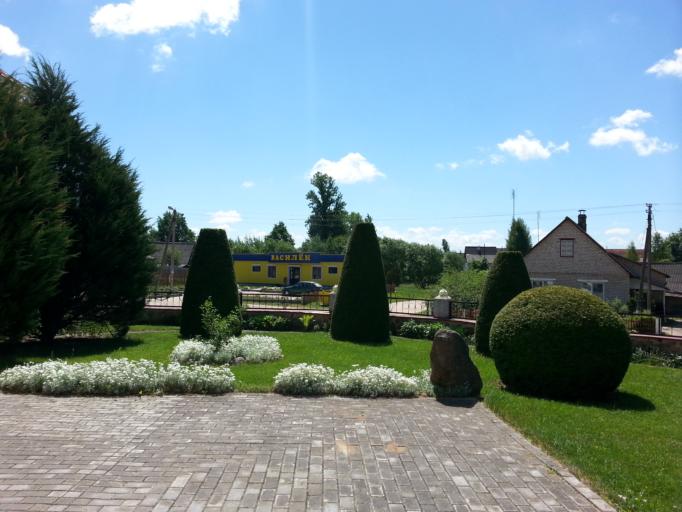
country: BY
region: Vitebsk
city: Mosar
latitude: 55.2105
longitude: 27.5592
